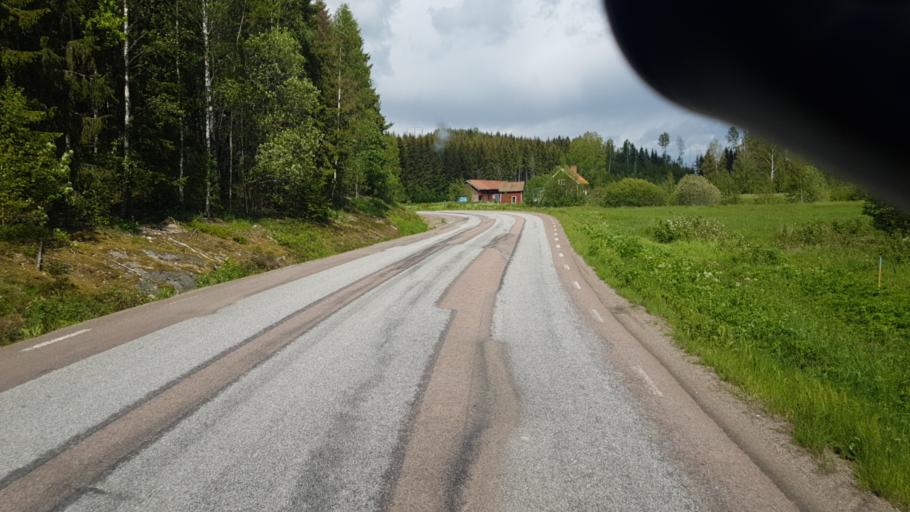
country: SE
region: Vaermland
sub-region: Arvika Kommun
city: Arvika
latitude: 59.6795
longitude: 12.4747
